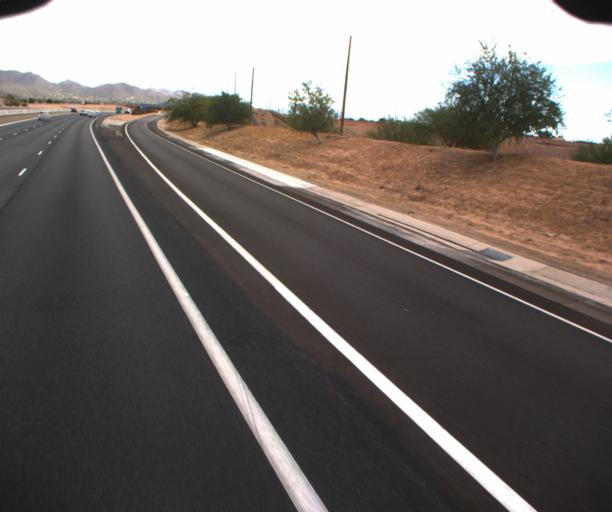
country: US
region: Arizona
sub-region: Maricopa County
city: Mesa
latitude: 33.4812
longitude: -111.7261
